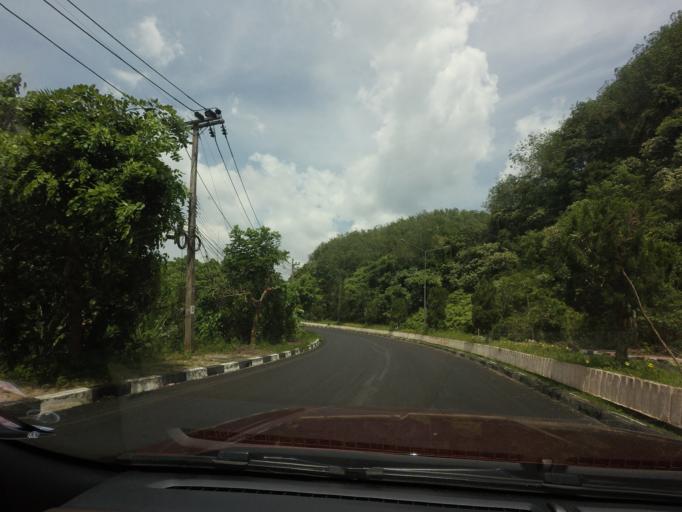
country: TH
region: Yala
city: Betong
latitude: 5.7596
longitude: 101.0452
